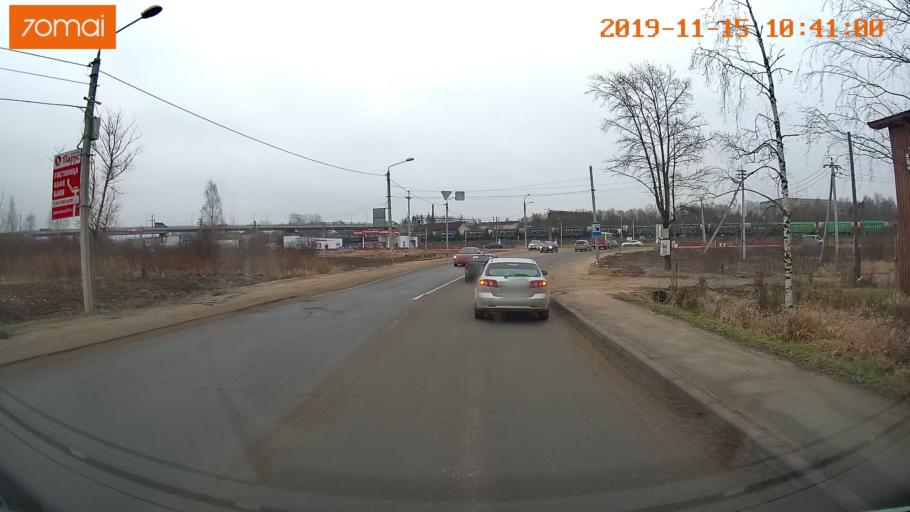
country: RU
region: Vologda
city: Sheksna
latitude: 59.2114
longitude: 38.5118
